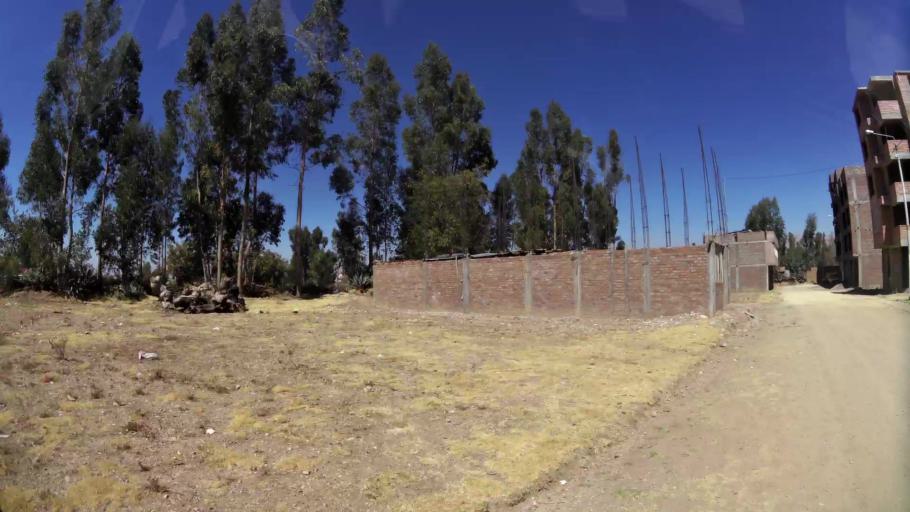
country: PE
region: Junin
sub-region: Provincia de Concepcion
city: Concepcion
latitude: -11.9160
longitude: -75.3224
